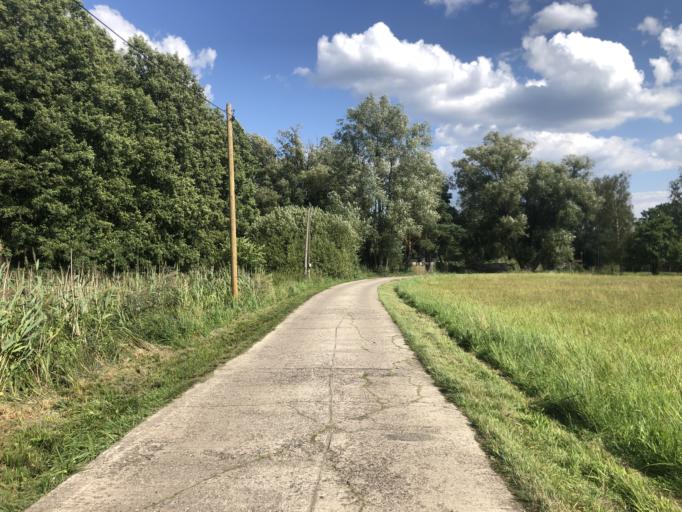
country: DE
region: Brandenburg
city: Mullrose
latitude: 52.2504
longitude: 14.4088
